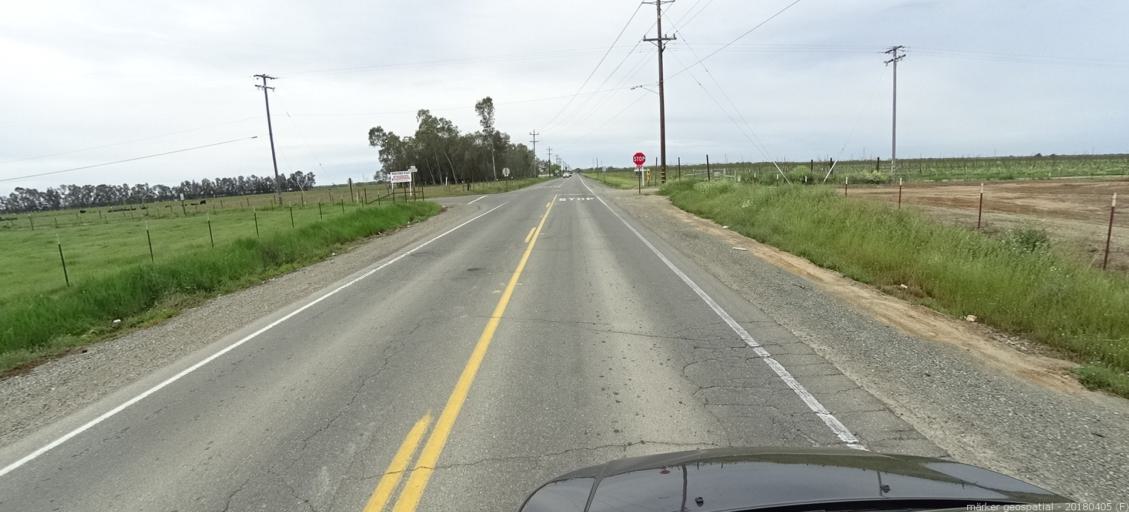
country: US
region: California
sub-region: Sacramento County
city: Galt
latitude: 38.2909
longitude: -121.3370
